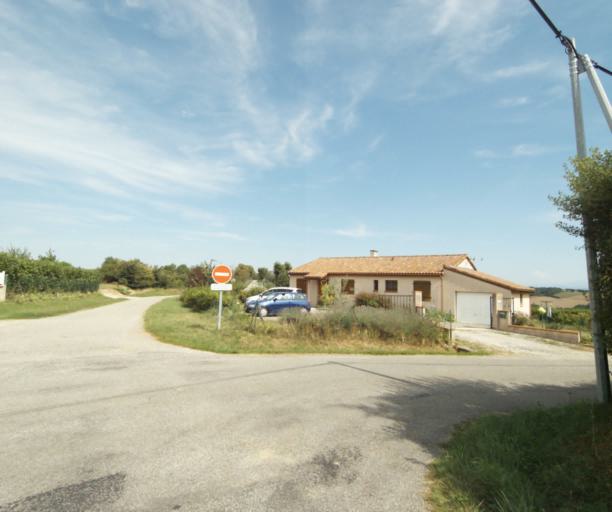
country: FR
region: Midi-Pyrenees
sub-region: Departement de l'Ariege
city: Lezat-sur-Leze
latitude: 43.2403
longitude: 1.3934
